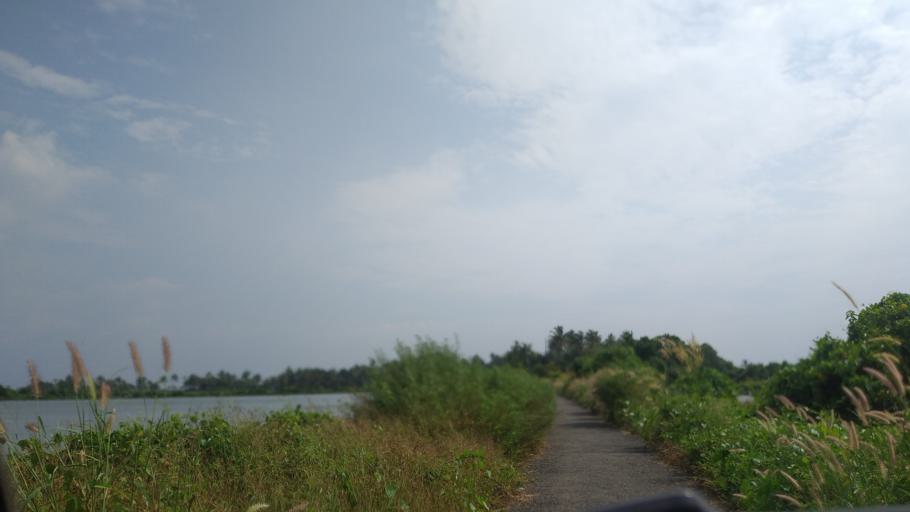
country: IN
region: Kerala
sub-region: Ernakulam
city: Elur
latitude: 10.0864
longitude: 76.2183
